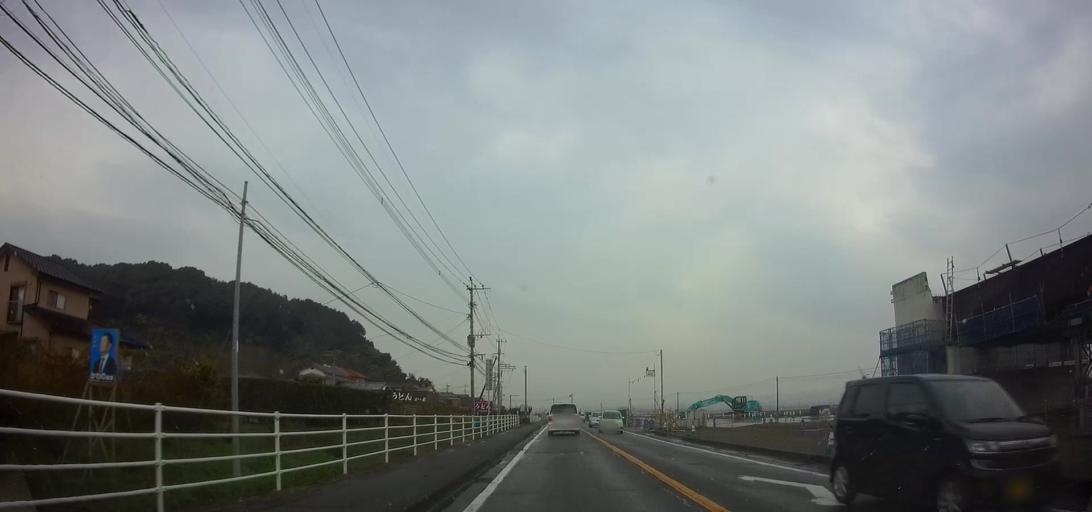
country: JP
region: Nagasaki
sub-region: Isahaya-shi
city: Isahaya
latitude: 32.8366
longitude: 130.1064
